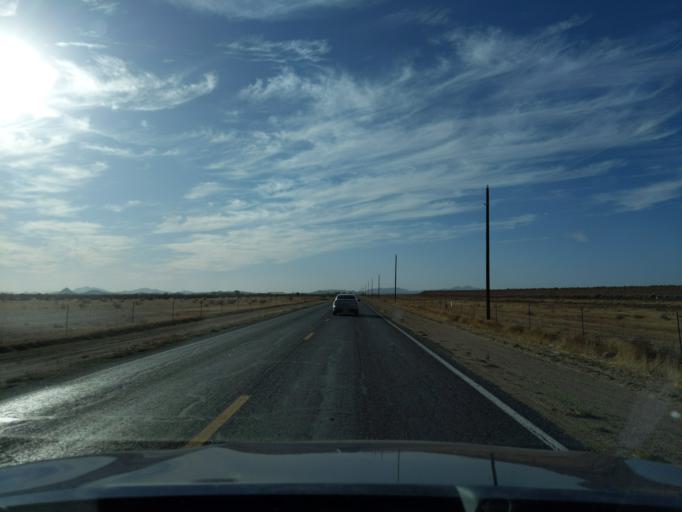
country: US
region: Arizona
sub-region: Pinal County
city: Florence
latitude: 33.1183
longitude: -111.3927
